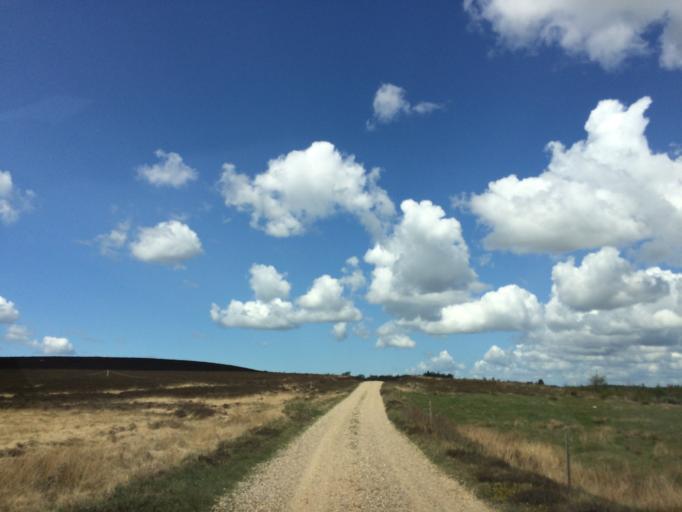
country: DK
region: Central Jutland
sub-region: Holstebro Kommune
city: Ulfborg
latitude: 56.2822
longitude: 8.4631
